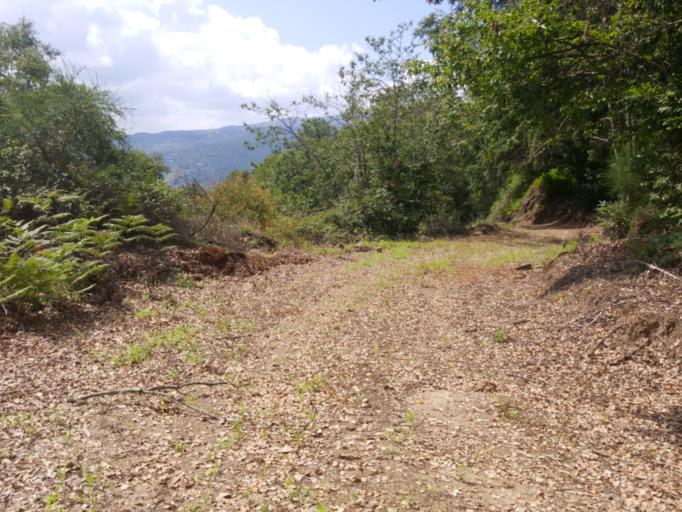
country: PT
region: Vila Real
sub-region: Mesao Frio
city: Mesao Frio
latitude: 41.1737
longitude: -7.8427
